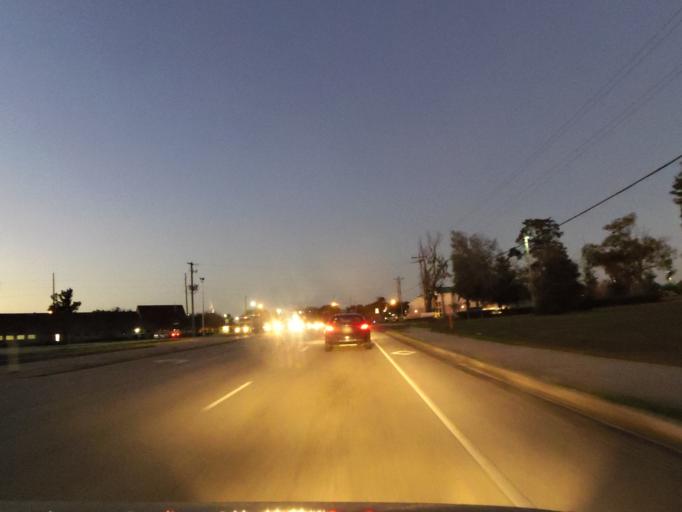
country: US
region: Florida
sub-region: Clay County
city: Lakeside
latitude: 30.1356
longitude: -81.7740
